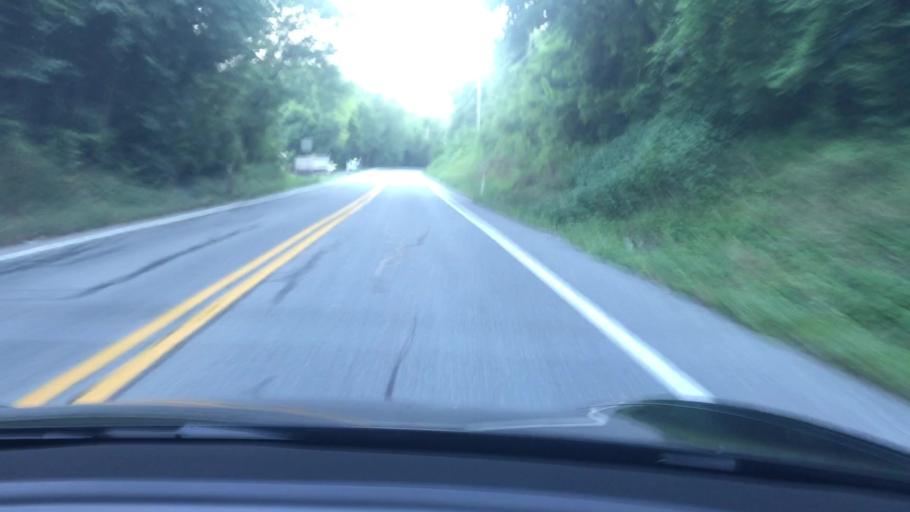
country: US
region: Pennsylvania
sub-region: York County
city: Dover
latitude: 40.0671
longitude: -76.8827
